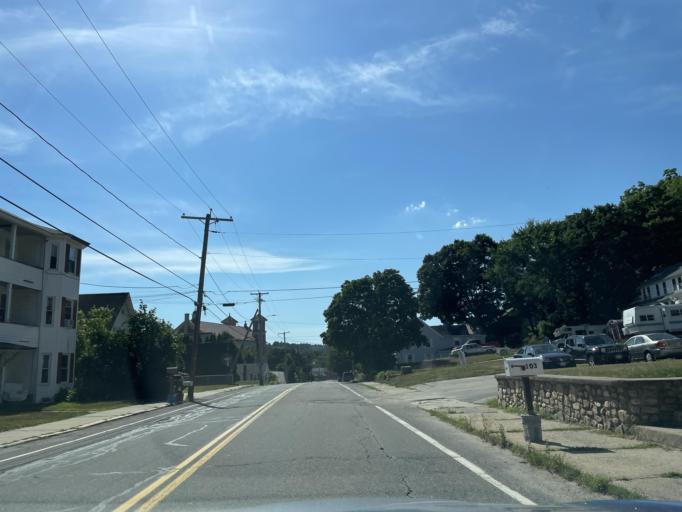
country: US
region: Massachusetts
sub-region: Worcester County
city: Northbridge
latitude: 42.1540
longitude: -71.6476
